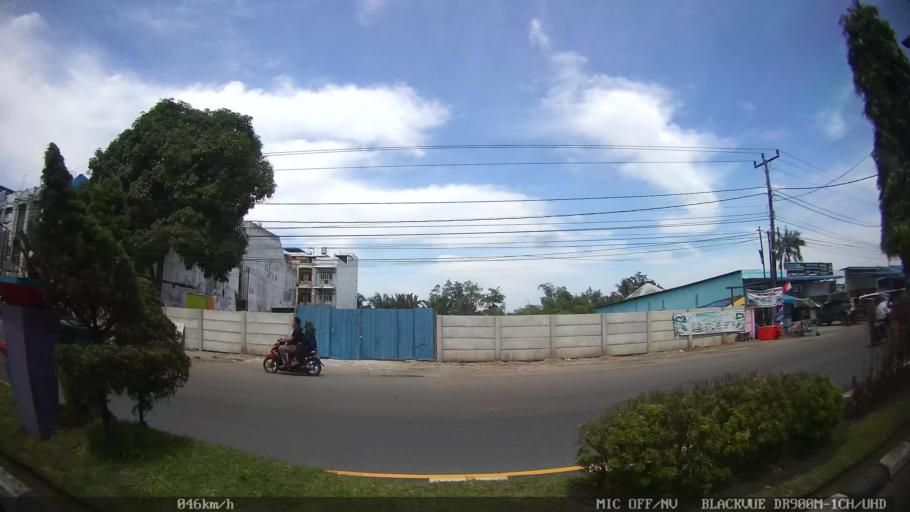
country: ID
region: North Sumatra
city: Binjai
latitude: 3.6125
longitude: 98.4954
